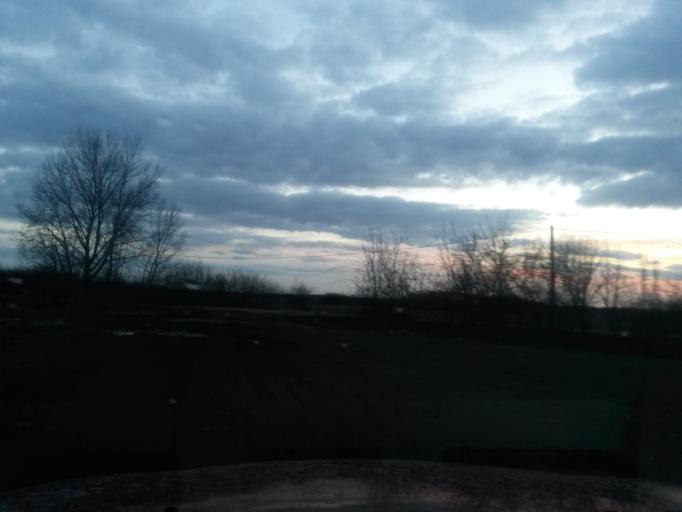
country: SK
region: Kosicky
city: Sobrance
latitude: 48.6902
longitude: 22.0520
